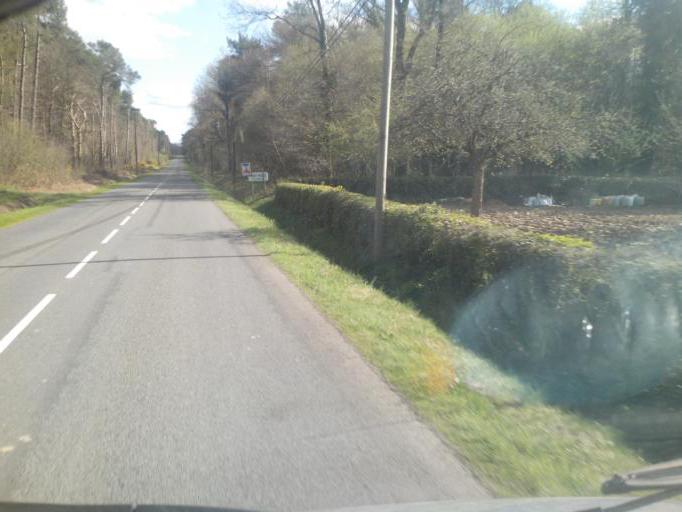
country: FR
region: Brittany
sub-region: Departement d'Ille-et-Vilaine
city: Paimpont
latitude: 48.0366
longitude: -2.1802
